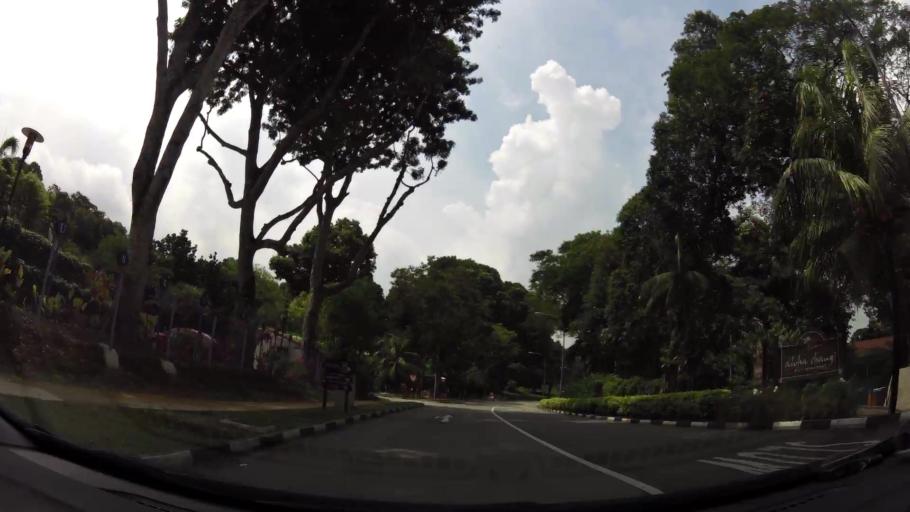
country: MY
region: Johor
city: Kampung Pasir Gudang Baru
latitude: 1.3914
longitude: 103.9825
